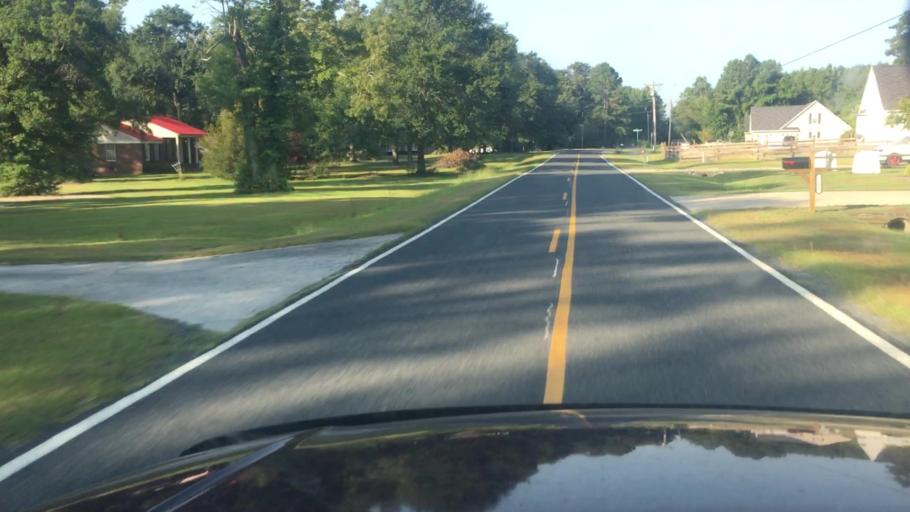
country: US
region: North Carolina
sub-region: Robeson County
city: Saint Pauls
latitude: 34.8428
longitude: -78.8884
